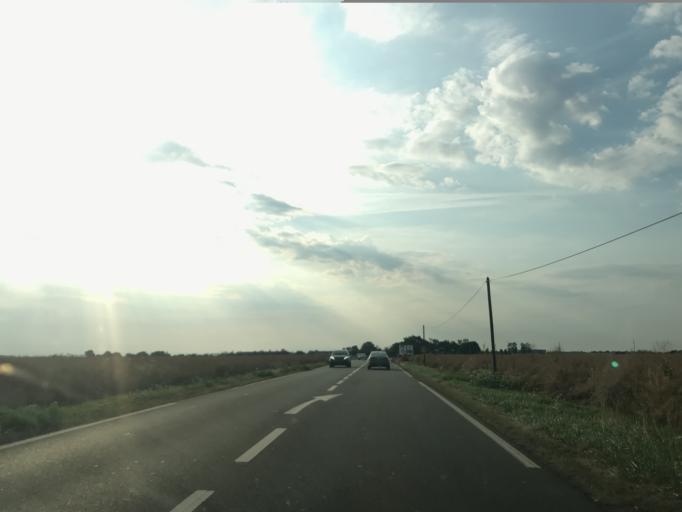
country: FR
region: Ile-de-France
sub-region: Departement de l'Essonne
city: Corbreuse
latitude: 48.4585
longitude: 1.9021
